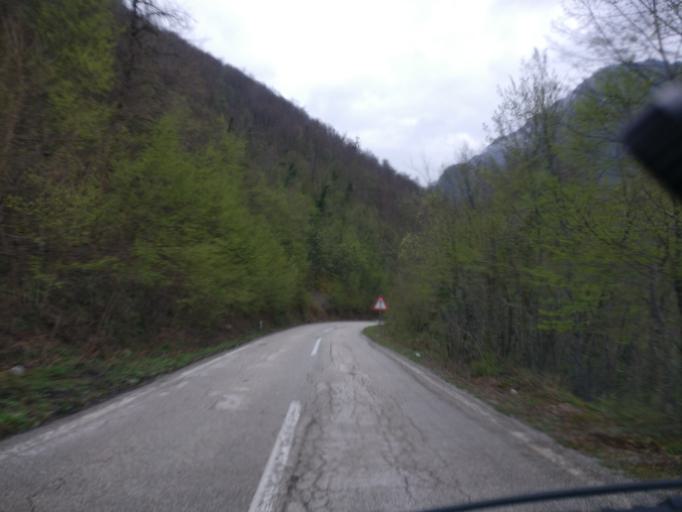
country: ME
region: Opstina Pluzine
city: Pluzine
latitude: 43.3134
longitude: 18.8562
